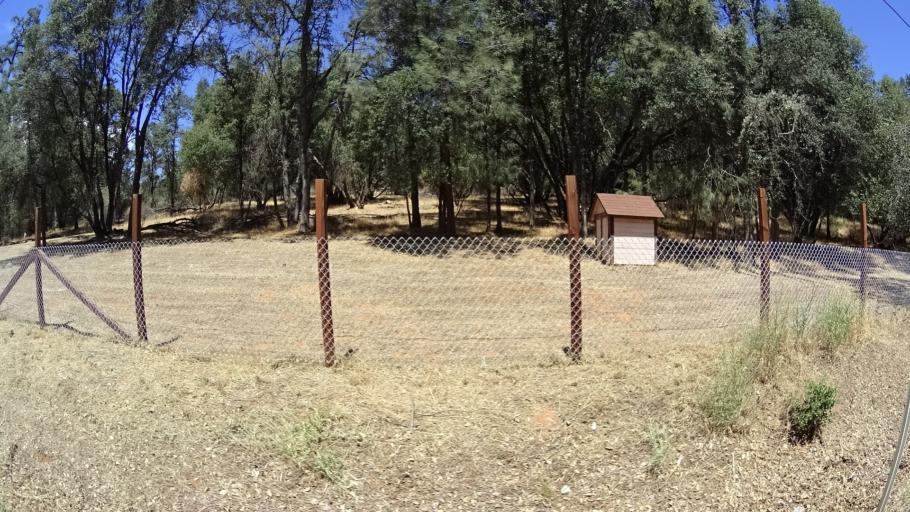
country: US
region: California
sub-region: Calaveras County
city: Mountain Ranch
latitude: 38.2258
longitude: -120.4903
